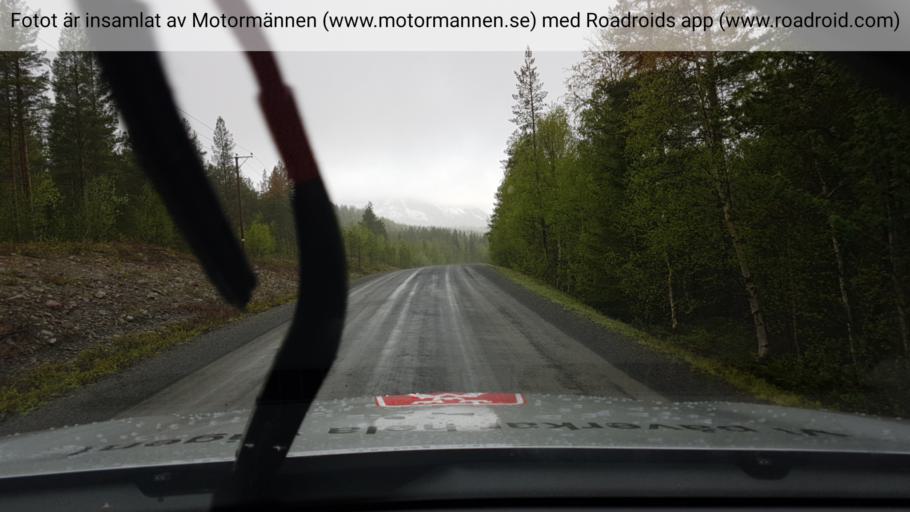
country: SE
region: Jaemtland
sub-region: Krokoms Kommun
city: Valla
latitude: 63.0808
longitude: 13.9366
